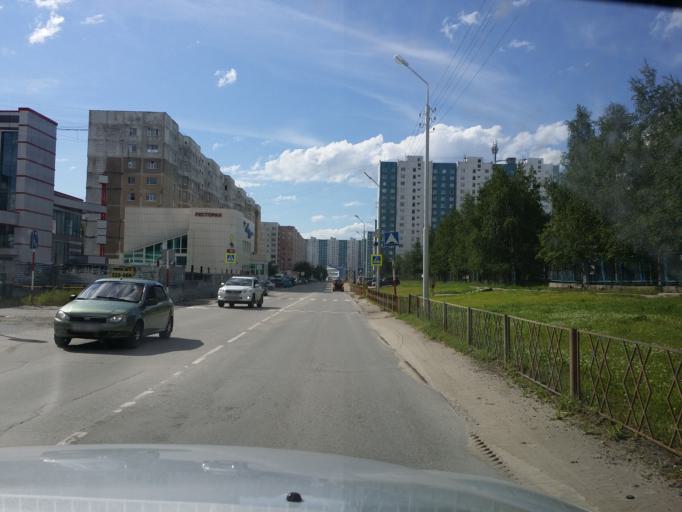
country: RU
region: Khanty-Mansiyskiy Avtonomnyy Okrug
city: Nizhnevartovsk
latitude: 60.9296
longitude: 76.6025
